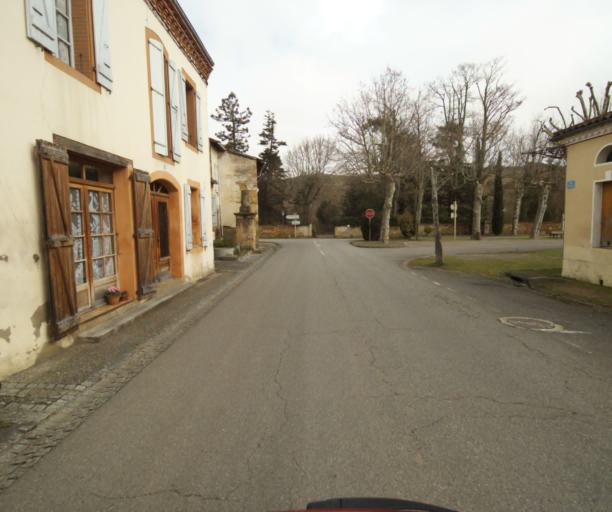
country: FR
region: Midi-Pyrenees
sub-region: Departement de la Haute-Garonne
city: Gaillac-Toulza
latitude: 43.1701
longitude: 1.4960
